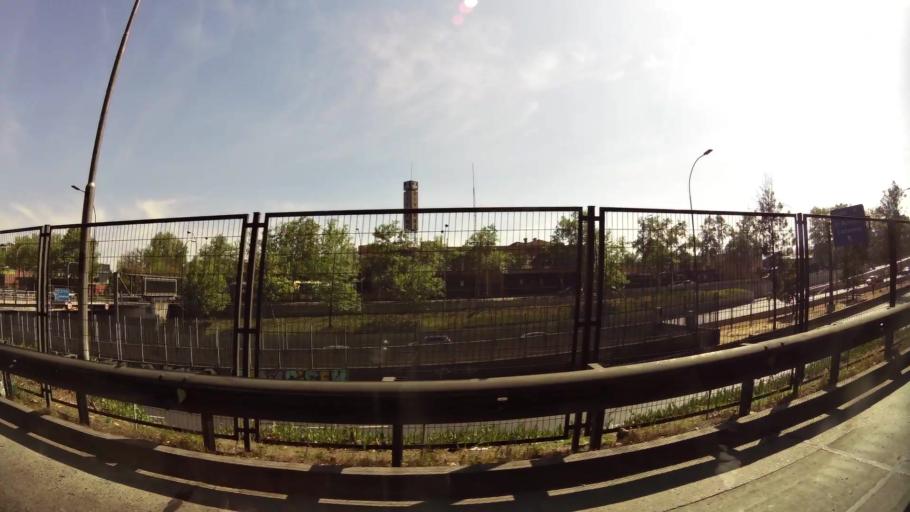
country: CL
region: Santiago Metropolitan
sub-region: Provincia de Santiago
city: Santiago
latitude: -33.4341
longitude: -70.6602
